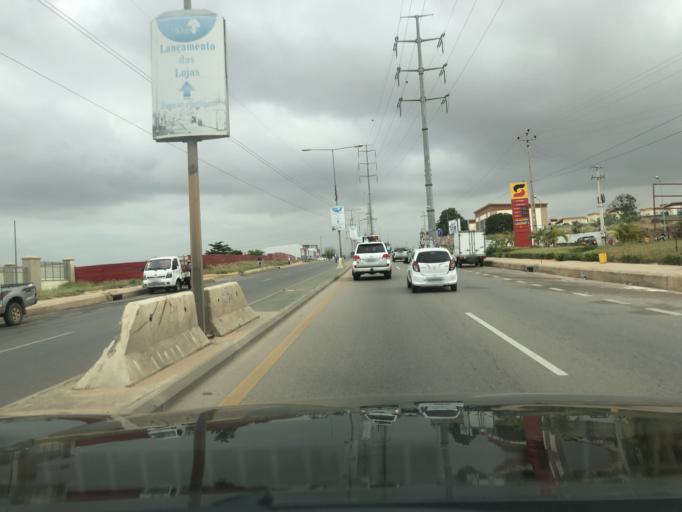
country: AO
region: Luanda
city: Luanda
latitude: -8.9653
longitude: 13.2054
